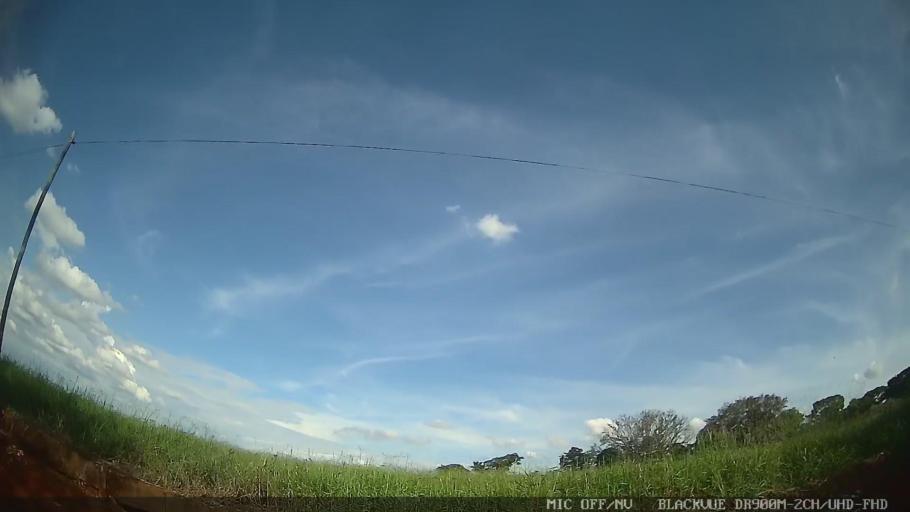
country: BR
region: Sao Paulo
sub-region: Jaguariuna
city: Jaguariuna
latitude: -22.6480
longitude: -47.0710
